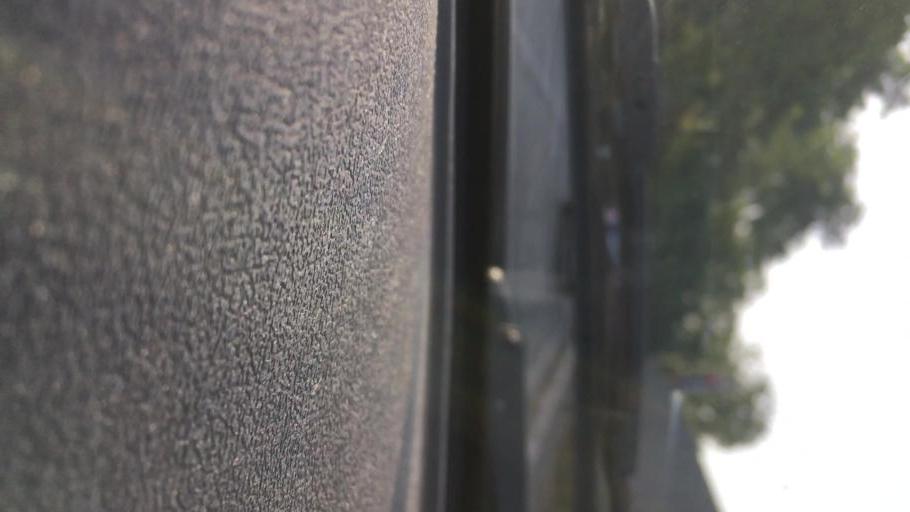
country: IT
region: Latium
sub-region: Citta metropolitana di Roma Capitale
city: Borgo Lotti
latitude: 41.8132
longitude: 12.5252
